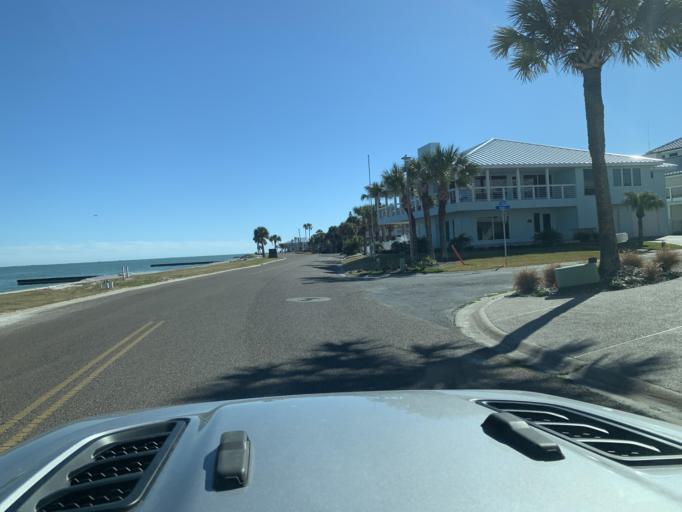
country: US
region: Texas
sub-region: Aransas County
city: Fulton
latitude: 28.0360
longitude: -97.0255
